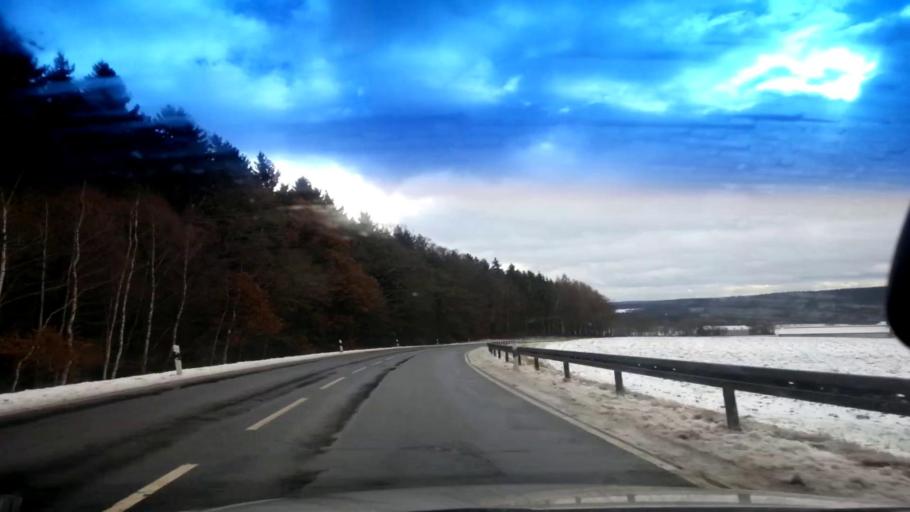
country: DE
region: Bavaria
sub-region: Upper Franconia
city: Kirchenlamitz
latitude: 50.1445
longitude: 11.9659
